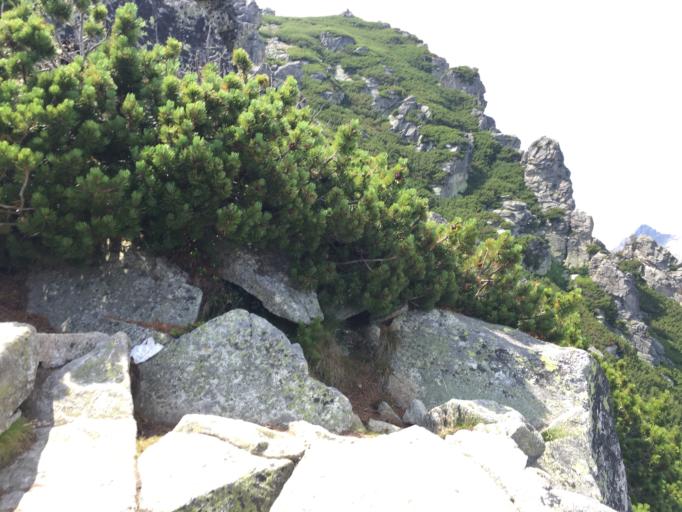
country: SK
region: Presovsky
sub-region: Okres Poprad
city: Vysoke Tatry
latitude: 49.1643
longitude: 20.2110
